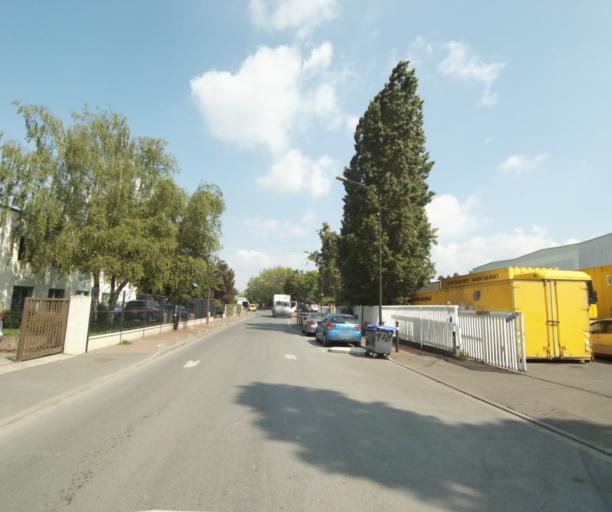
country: FR
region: Ile-de-France
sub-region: Departement des Yvelines
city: Sartrouville
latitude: 48.9488
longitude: 2.2096
